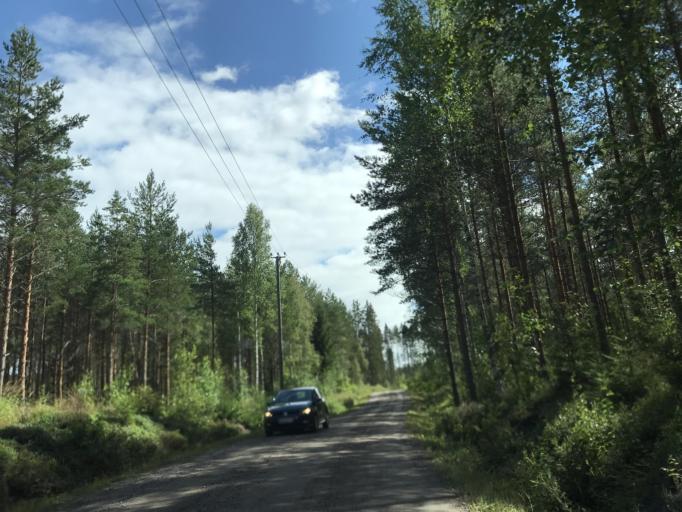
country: FI
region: Uusimaa
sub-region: Helsinki
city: Kaerkoelae
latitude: 60.6378
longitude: 23.8245
